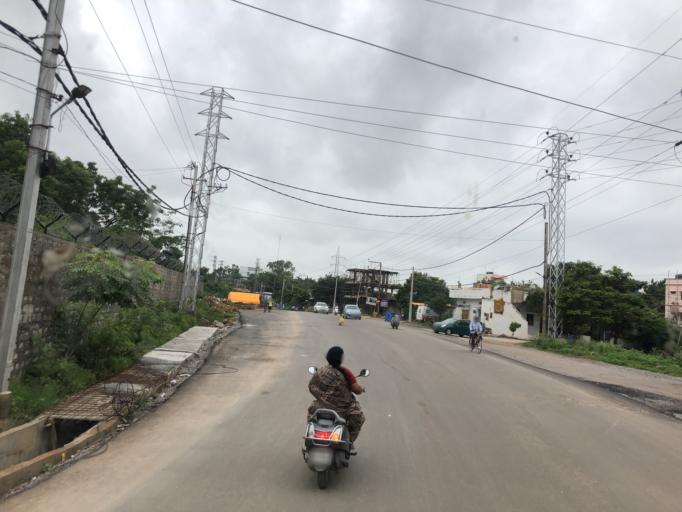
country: IN
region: Telangana
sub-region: Medak
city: Serilingampalle
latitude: 17.4684
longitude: 78.3335
